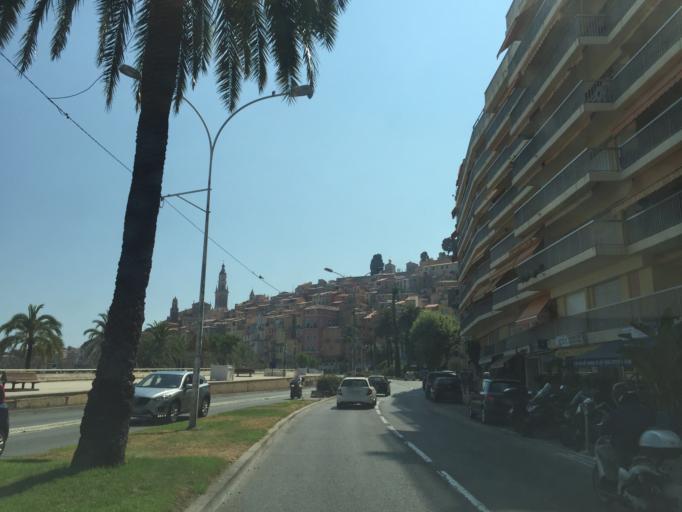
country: FR
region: Provence-Alpes-Cote d'Azur
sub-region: Departement des Alpes-Maritimes
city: Menton
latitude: 43.7805
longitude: 7.5089
